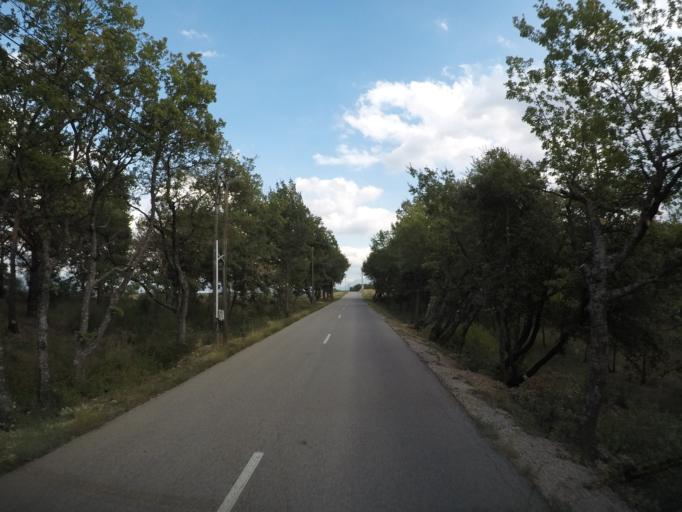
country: FR
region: Provence-Alpes-Cote d'Azur
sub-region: Departement des Alpes-de-Haute-Provence
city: Valensole
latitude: 43.8344
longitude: 6.0222
